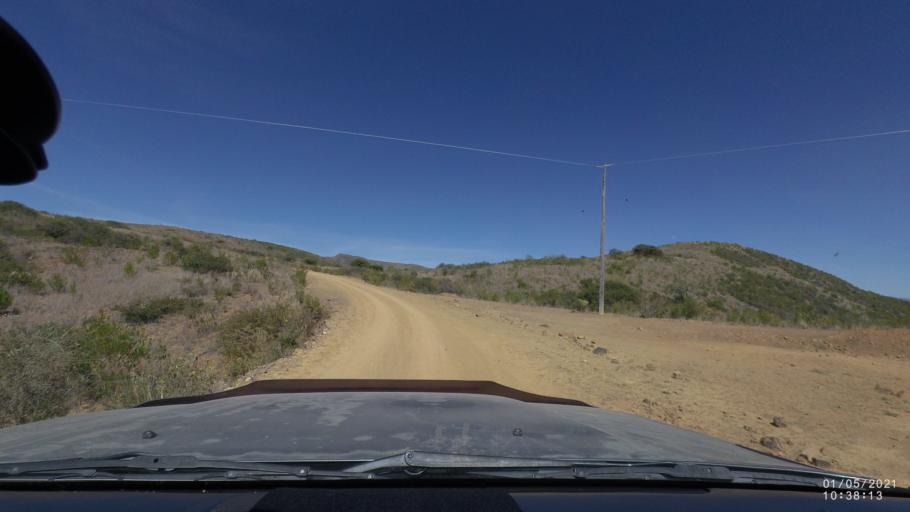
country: BO
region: Cochabamba
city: Capinota
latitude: -17.6034
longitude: -66.1853
